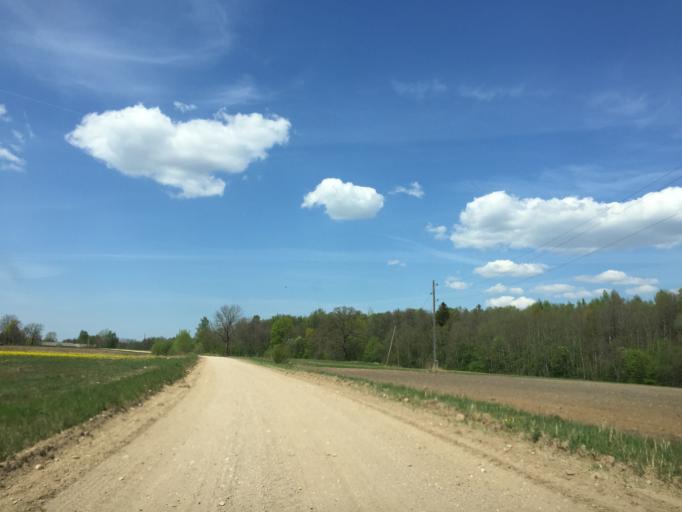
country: LV
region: Limbazu Rajons
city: Limbazi
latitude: 57.3787
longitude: 24.6264
